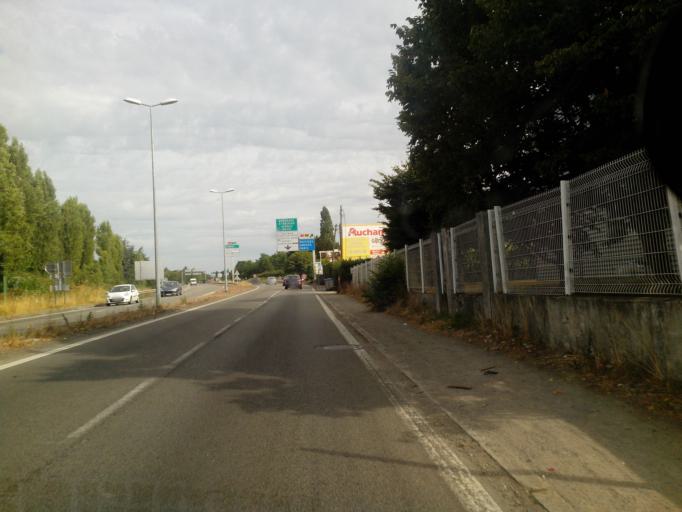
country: FR
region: Pays de la Loire
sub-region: Departement de la Loire-Atlantique
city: Orvault
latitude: 47.2626
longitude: -1.5837
